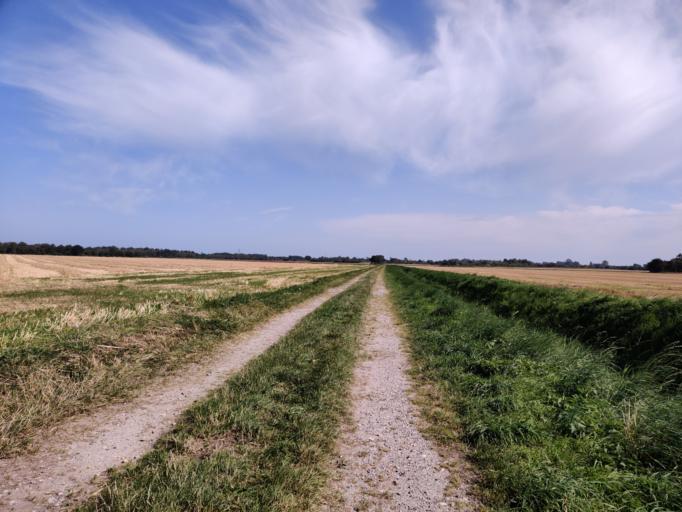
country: DK
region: Zealand
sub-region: Guldborgsund Kommune
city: Nykobing Falster
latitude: 54.6810
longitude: 11.9163
